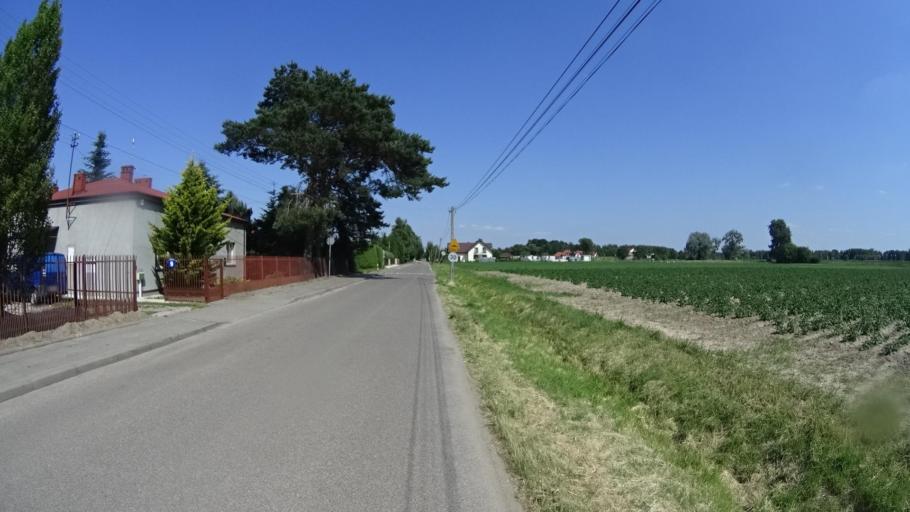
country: PL
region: Masovian Voivodeship
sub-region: Powiat warszawski zachodni
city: Bieniewice
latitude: 52.1910
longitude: 20.5439
